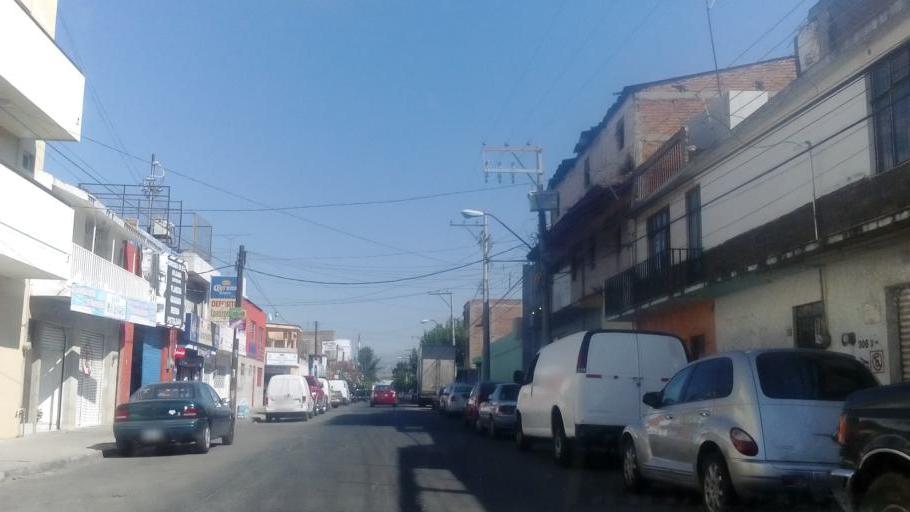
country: MX
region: Guanajuato
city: Leon
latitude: 21.1333
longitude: -101.6870
